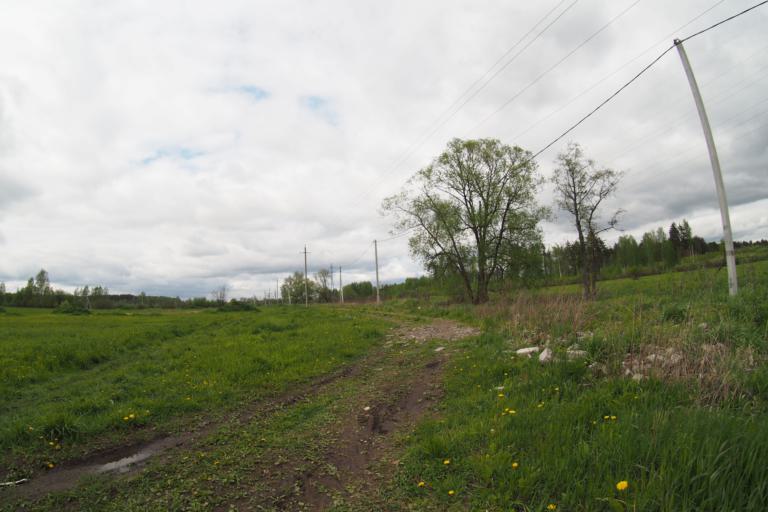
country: RU
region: Moskovskaya
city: Rechitsy
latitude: 55.5613
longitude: 38.4824
